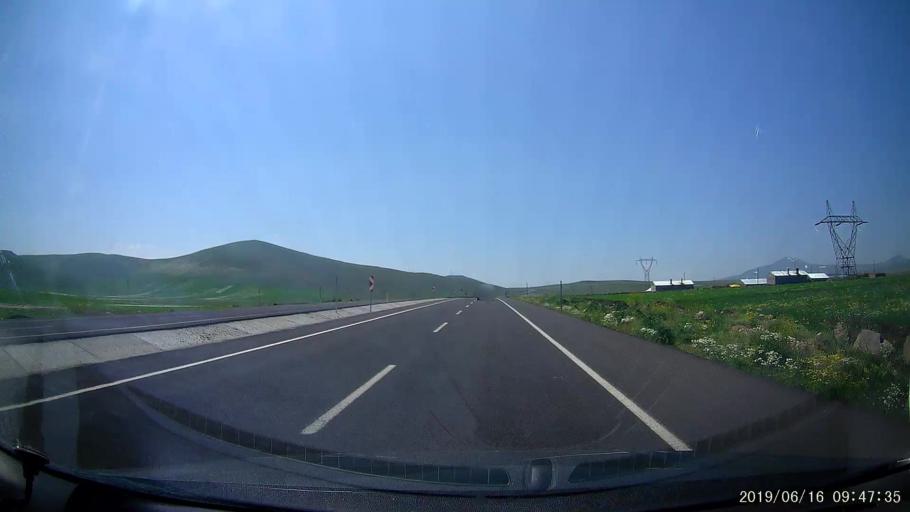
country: TR
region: Kars
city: Digor
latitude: 40.4448
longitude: 43.3455
